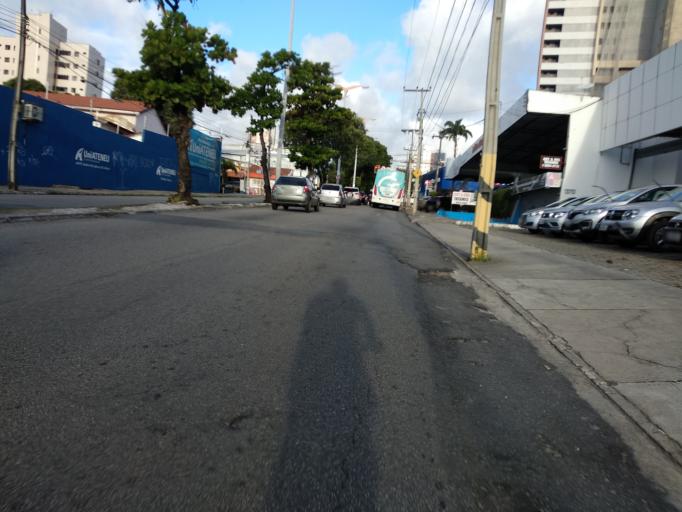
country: BR
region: Ceara
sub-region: Fortaleza
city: Fortaleza
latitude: -3.7373
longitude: -38.5131
